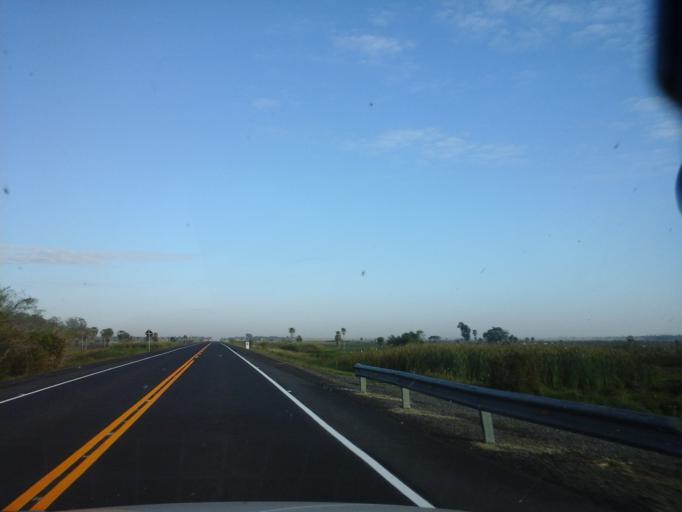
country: PY
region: Neembucu
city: Cerrito
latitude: -26.8670
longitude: -57.8150
